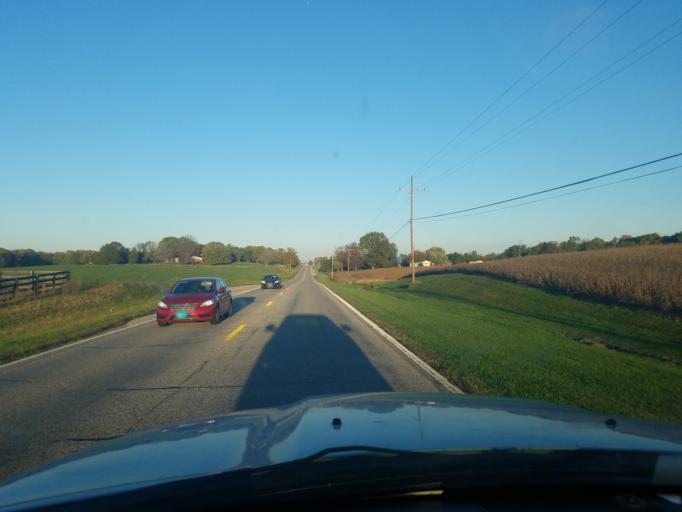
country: US
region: Indiana
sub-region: Floyd County
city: Galena
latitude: 38.3873
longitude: -86.0396
